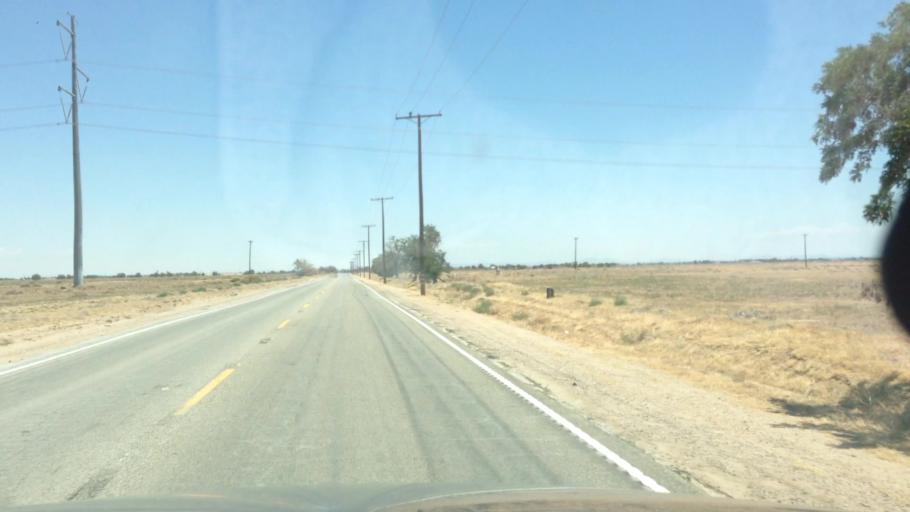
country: US
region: California
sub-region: Los Angeles County
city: Leona Valley
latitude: 34.7762
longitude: -118.3196
